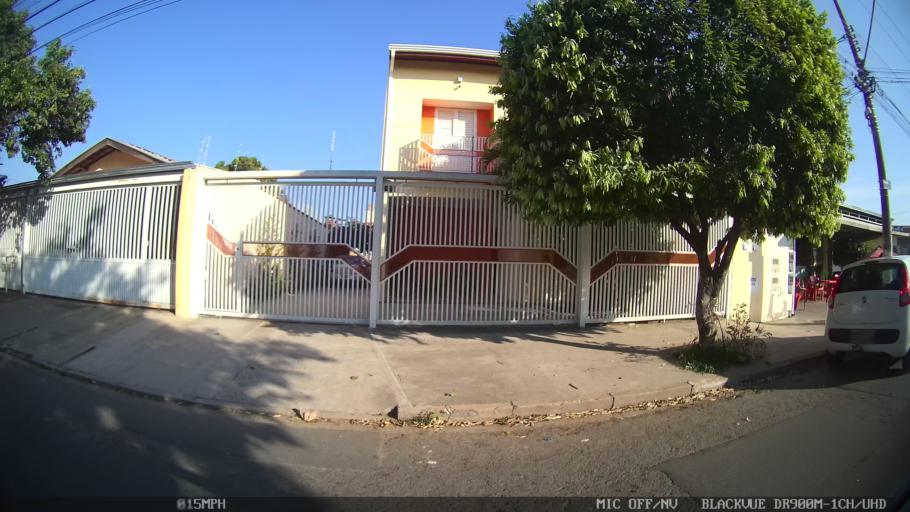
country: BR
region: Sao Paulo
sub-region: Campinas
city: Campinas
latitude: -22.9704
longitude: -47.1480
